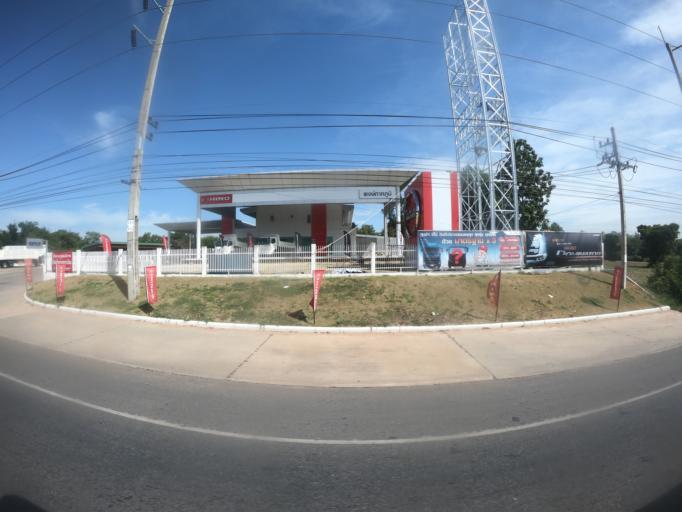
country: TH
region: Maha Sarakham
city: Chiang Yuen
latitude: 16.4420
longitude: 102.9719
